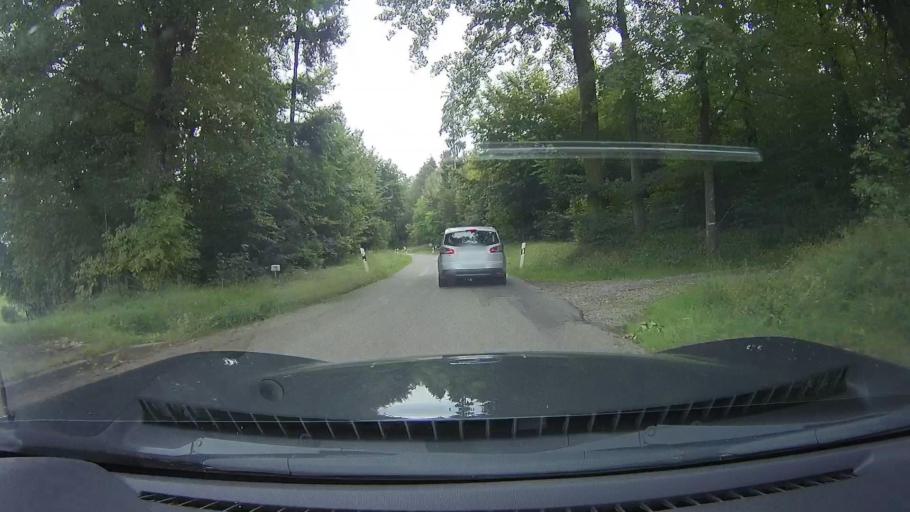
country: DE
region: Baden-Wuerttemberg
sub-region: Regierungsbezirk Stuttgart
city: Murrhardt
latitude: 49.0203
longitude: 9.5627
